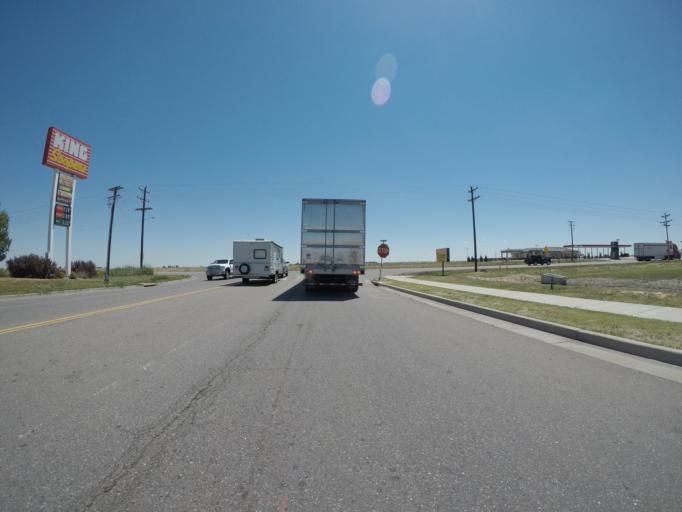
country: US
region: Colorado
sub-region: Adams County
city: Bennett
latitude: 39.7421
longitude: -104.4340
